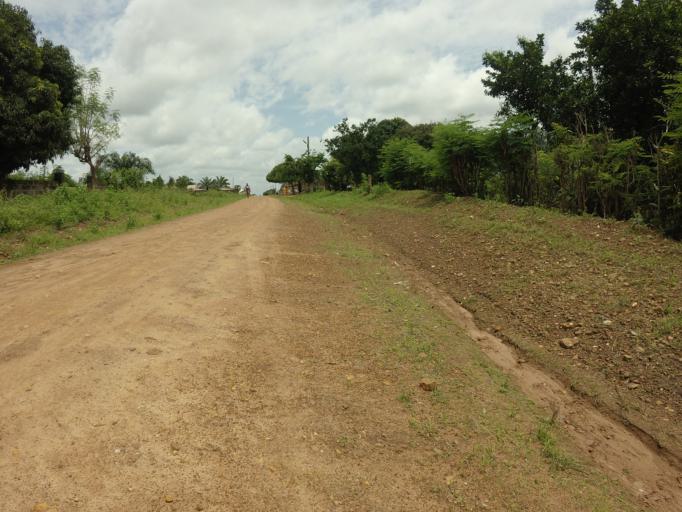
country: GH
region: Volta
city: Ho
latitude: 6.5779
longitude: 0.4598
